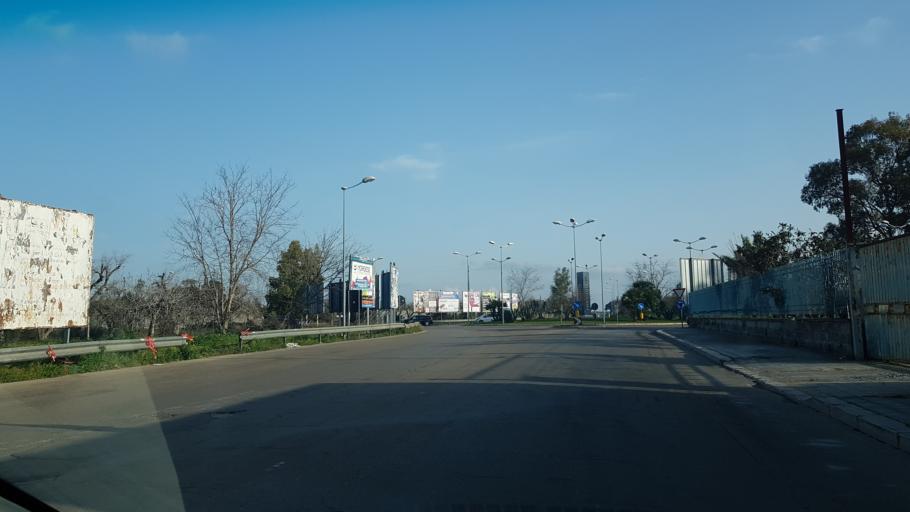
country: IT
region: Apulia
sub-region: Provincia di Lecce
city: Squinzano
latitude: 40.4283
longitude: 18.0525
